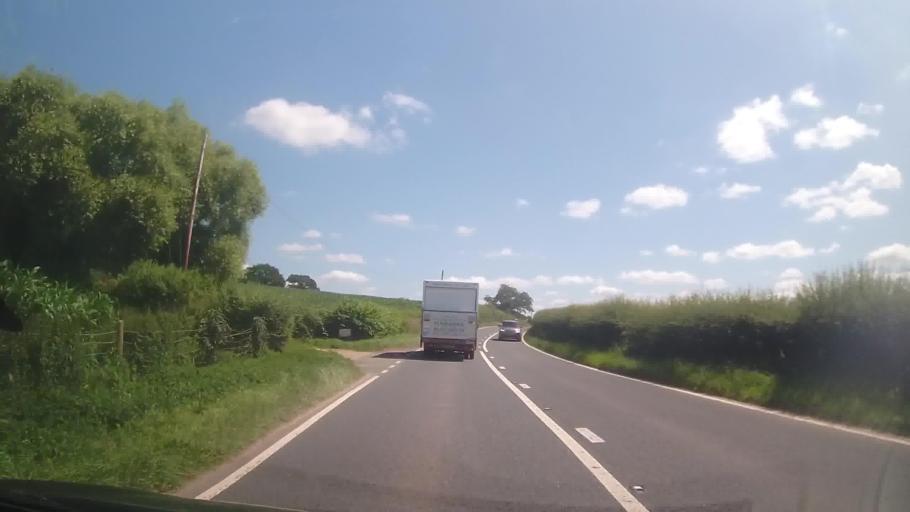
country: GB
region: England
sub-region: Herefordshire
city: Ocle Pychard
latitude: 52.1457
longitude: -2.6308
